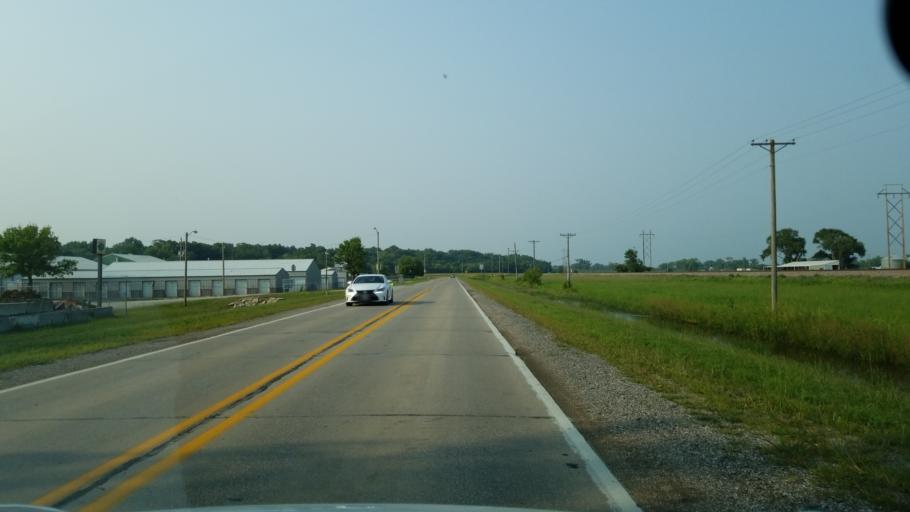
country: US
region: Nebraska
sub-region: Sarpy County
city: Bellevue
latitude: 41.1225
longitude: -95.8901
